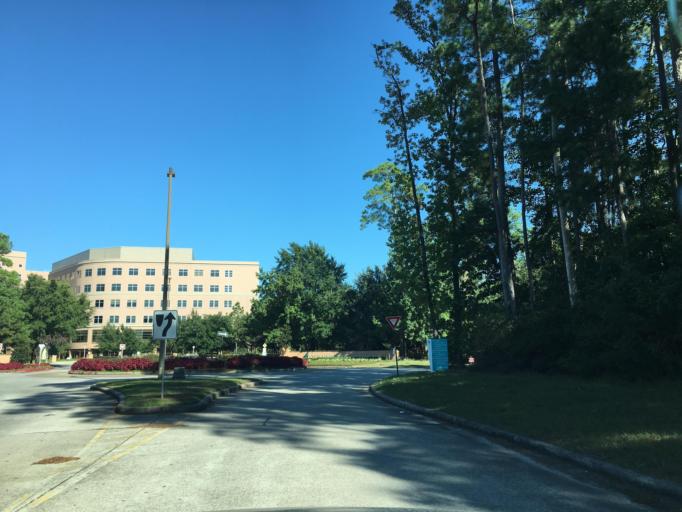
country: US
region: Texas
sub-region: Montgomery County
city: Shenandoah
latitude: 30.2049
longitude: -95.4601
